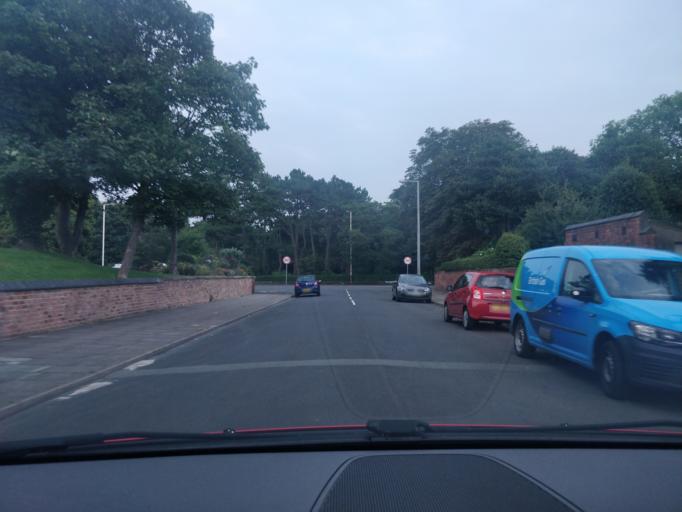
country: GB
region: England
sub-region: Sefton
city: Southport
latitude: 53.6587
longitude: -2.9881
